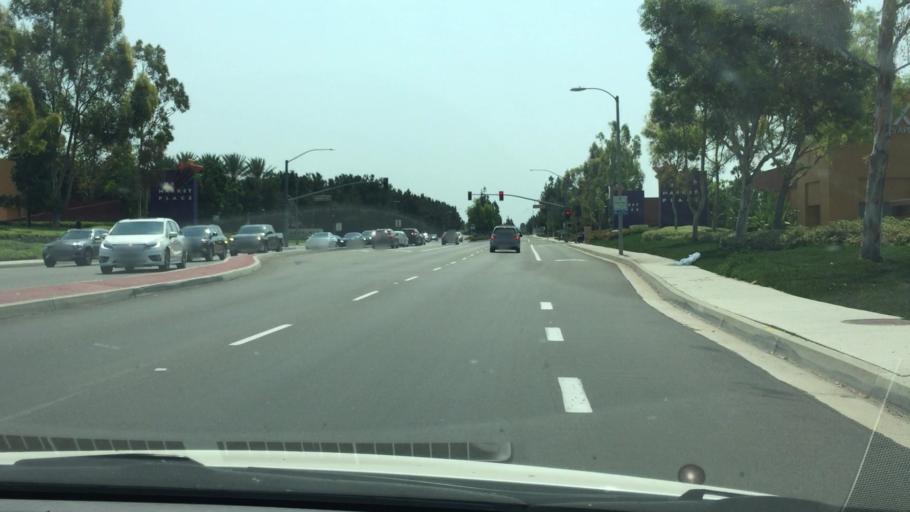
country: US
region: California
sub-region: Orange County
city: North Tustin
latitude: 33.7248
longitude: -117.7902
